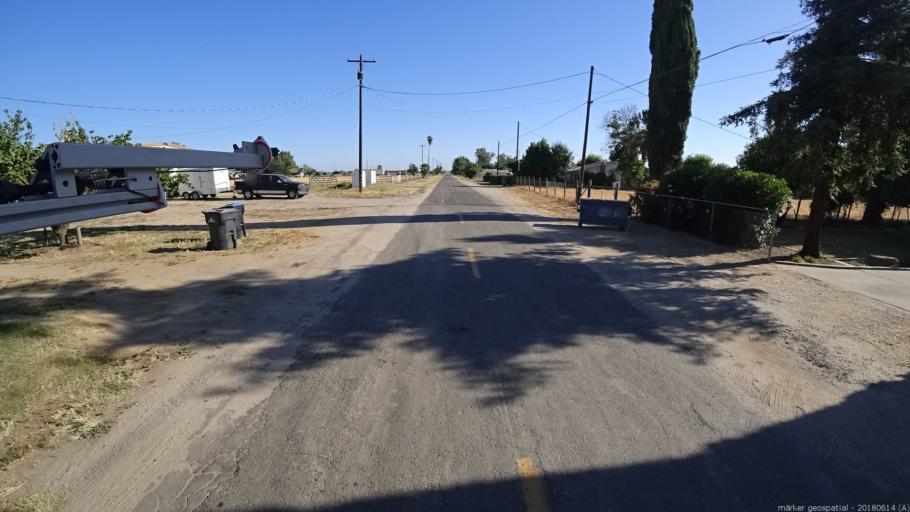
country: US
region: California
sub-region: Madera County
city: Madera
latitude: 36.9560
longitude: -120.1194
